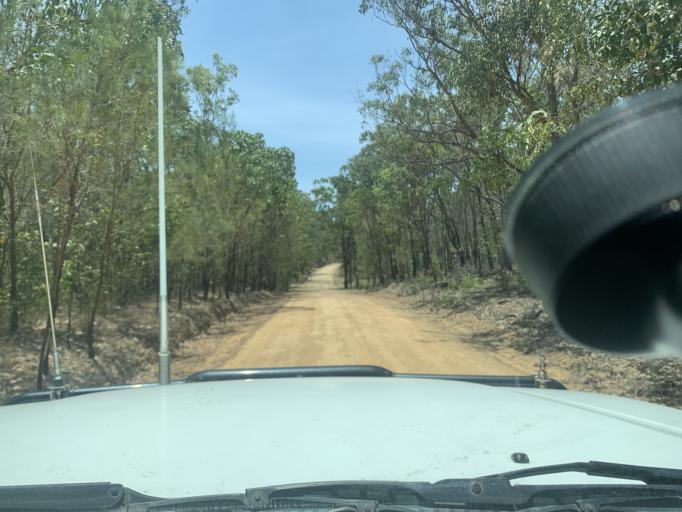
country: AU
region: Queensland
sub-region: Tablelands
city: Kuranda
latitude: -16.9184
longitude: 145.5959
